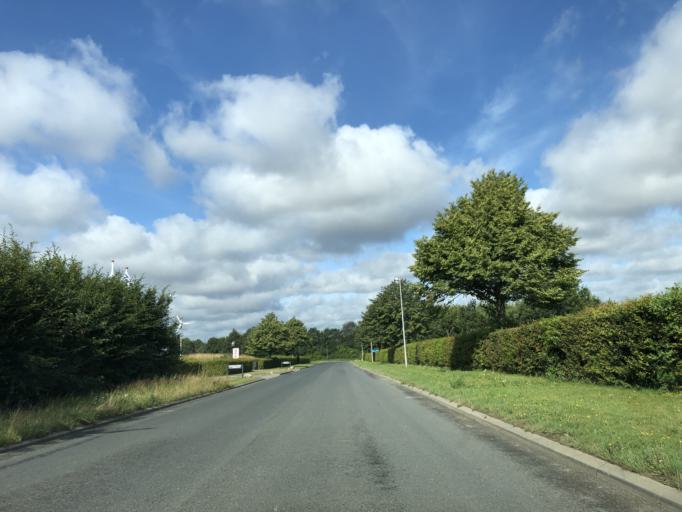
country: DK
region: Central Jutland
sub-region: Silkeborg Kommune
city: Silkeborg
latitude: 56.2015
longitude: 9.5893
